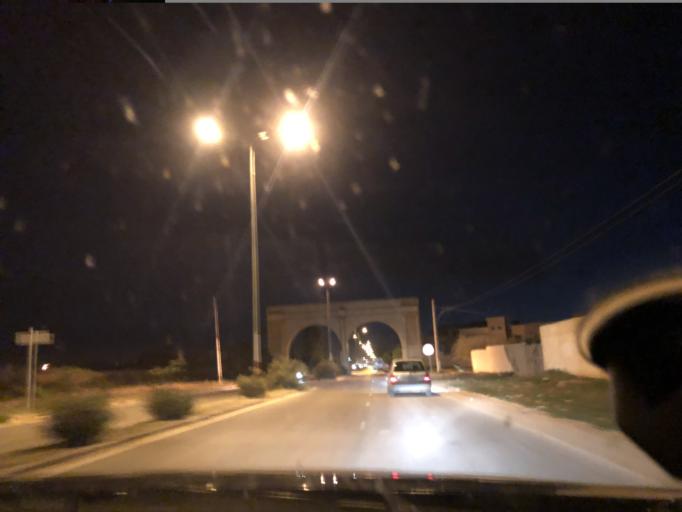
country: TN
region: Al Qasrayn
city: Kasserine
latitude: 35.1830
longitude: 8.8600
